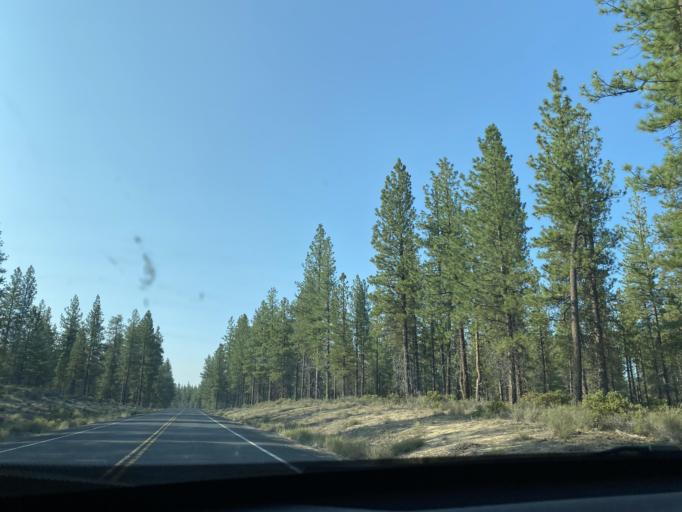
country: US
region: Oregon
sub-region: Deschutes County
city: La Pine
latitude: 43.7171
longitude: -121.4135
